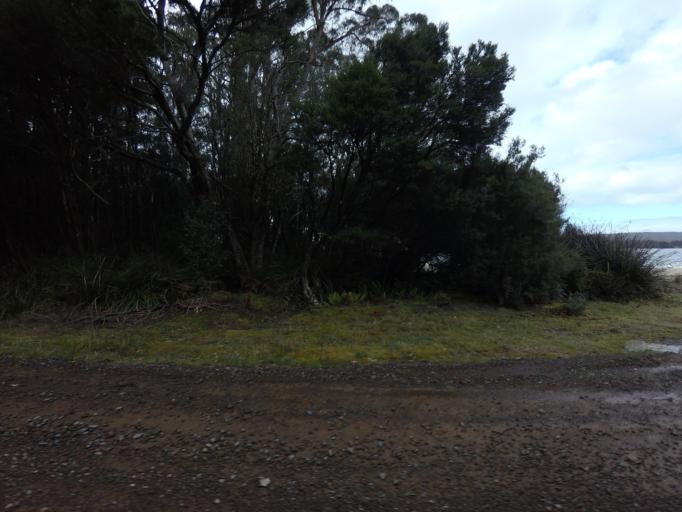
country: AU
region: Tasmania
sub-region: Huon Valley
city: Geeveston
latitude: -43.5421
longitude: 146.8922
